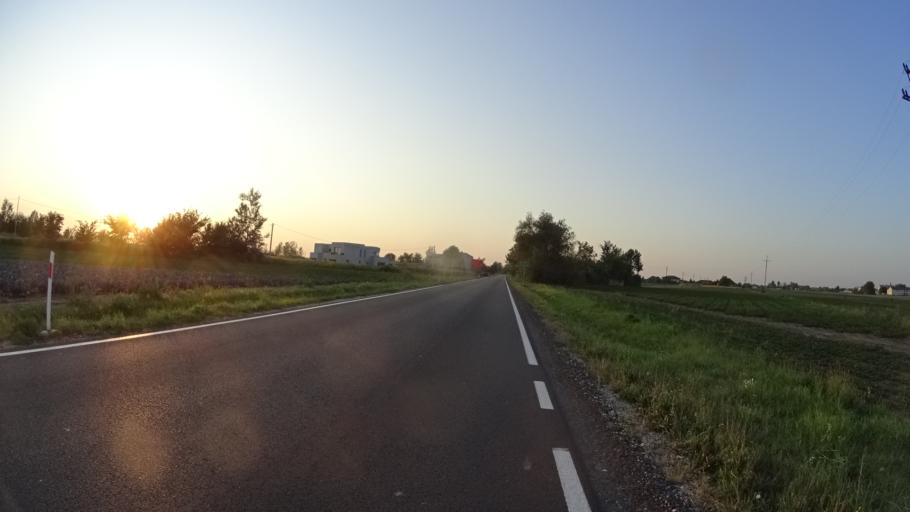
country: PL
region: Masovian Voivodeship
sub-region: Powiat warszawski zachodni
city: Ozarow Mazowiecki
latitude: 52.2420
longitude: 20.7498
